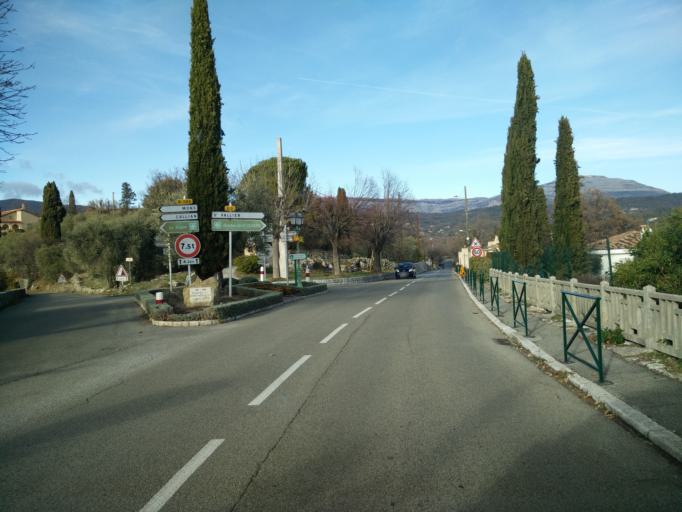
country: FR
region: Provence-Alpes-Cote d'Azur
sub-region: Departement des Alpes-Maritimes
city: Saint-Cezaire-sur-Siagne
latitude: 43.6525
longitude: 6.7913
